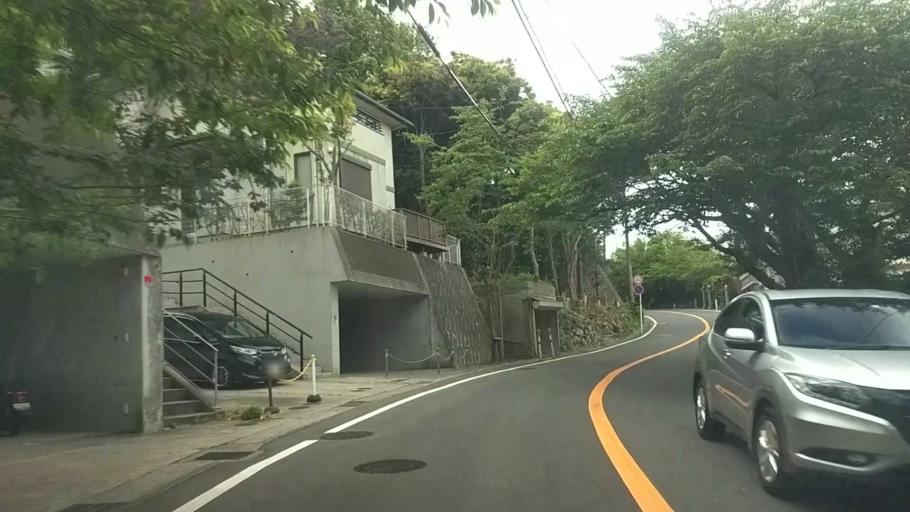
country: JP
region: Kanagawa
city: Kamakura
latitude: 35.3202
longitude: 139.5138
